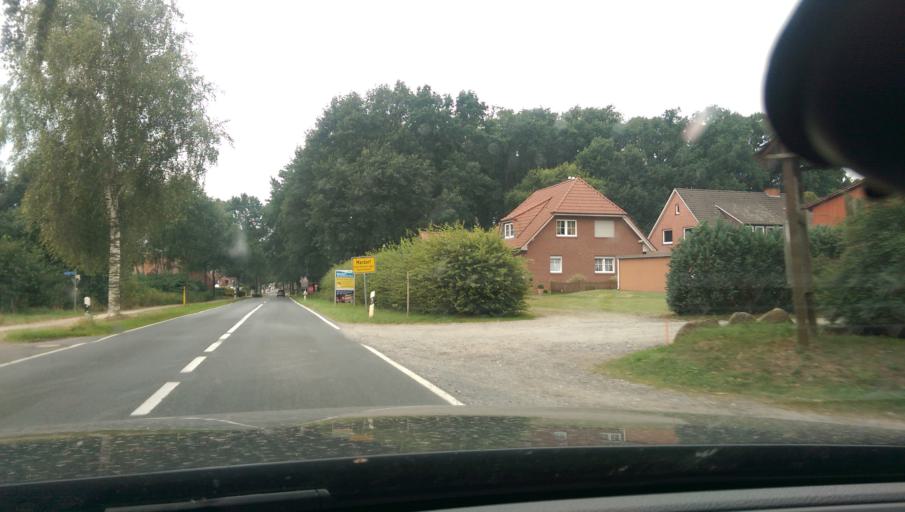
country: DE
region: Lower Saxony
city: Hagenburg
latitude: 52.4939
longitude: 9.2957
